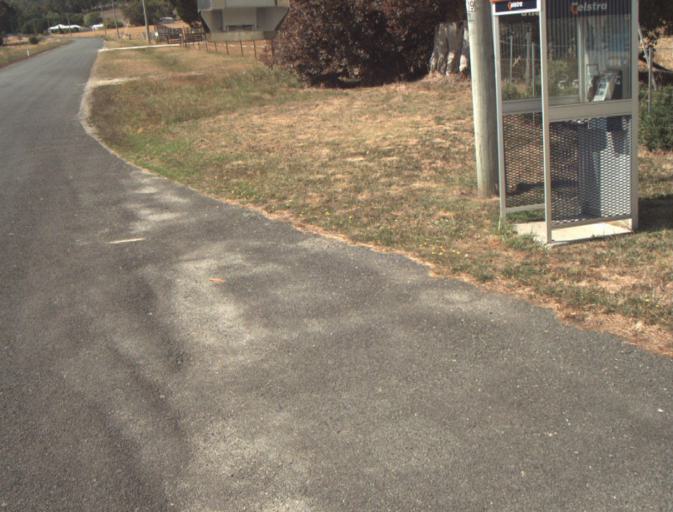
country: AU
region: Tasmania
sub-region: Launceston
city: Mayfield
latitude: -41.2576
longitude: 147.1532
